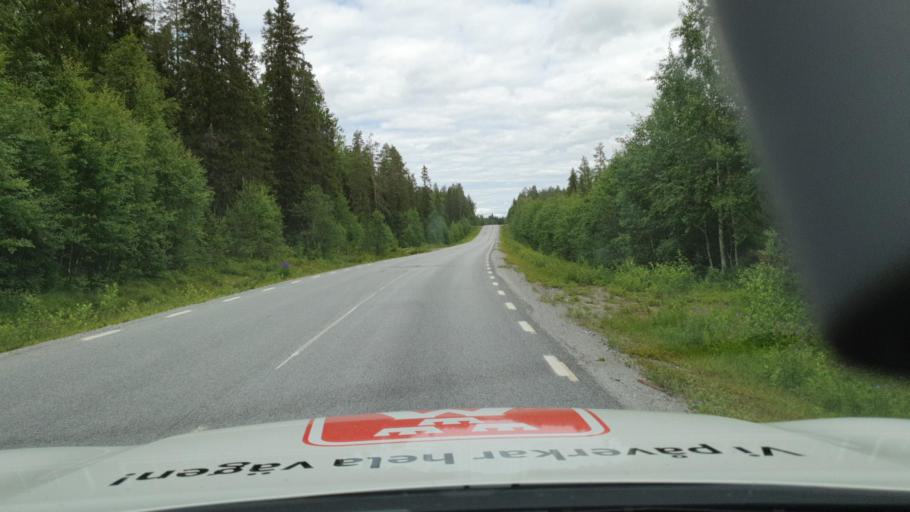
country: SE
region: Vaesterbotten
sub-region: Bjurholms Kommun
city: Bjurholm
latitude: 63.8884
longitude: 19.0623
